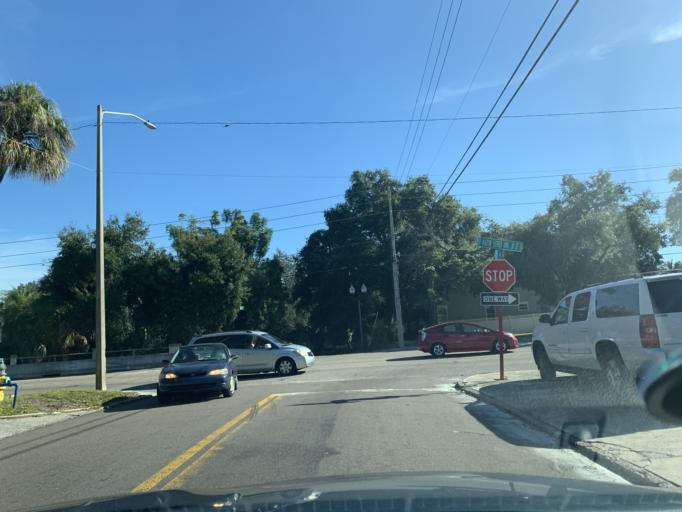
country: US
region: Florida
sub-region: Pinellas County
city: Saint Petersburg
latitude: 27.7631
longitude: -82.6469
